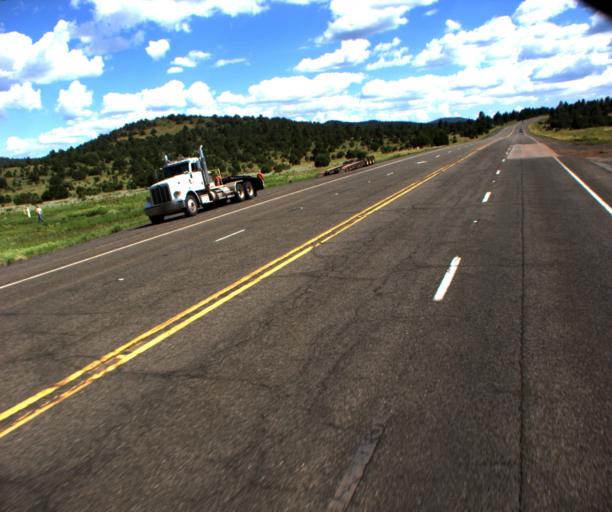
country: US
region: Arizona
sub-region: Coconino County
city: Williams
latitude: 35.3051
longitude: -112.1444
